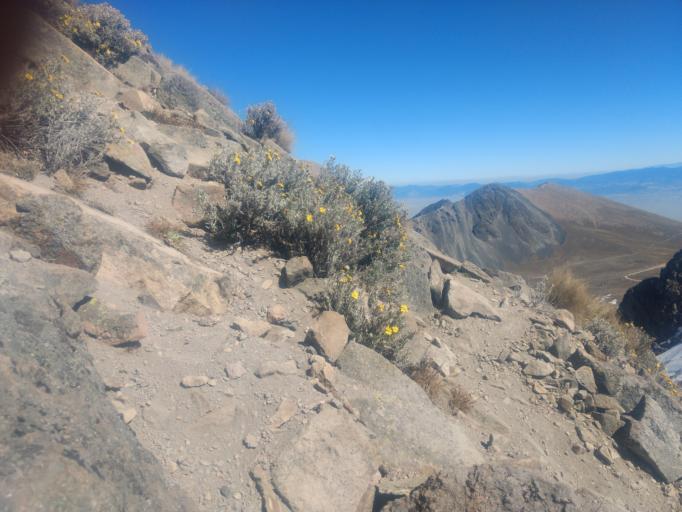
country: MX
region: Mexico
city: Cerro La Calera
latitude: 19.1015
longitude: -99.7627
